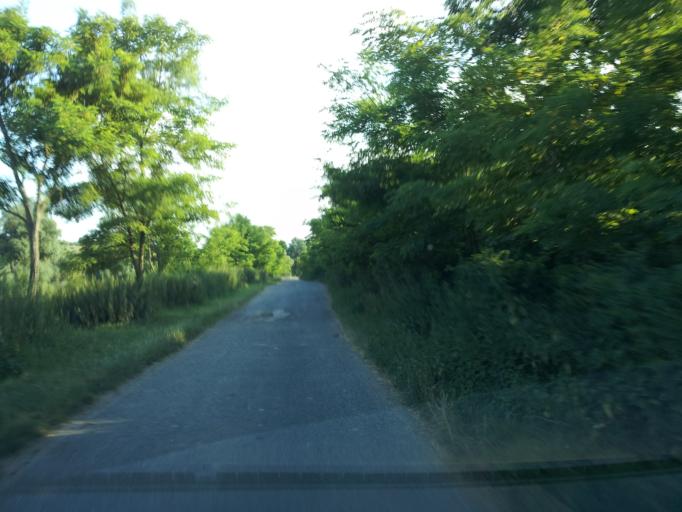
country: HU
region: Fejer
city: Many
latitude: 47.5621
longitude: 18.5968
